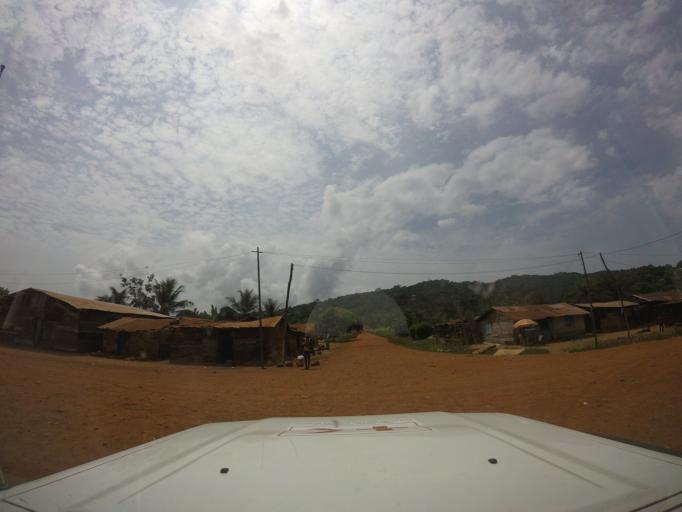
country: LR
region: Grand Cape Mount
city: Robertsport
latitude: 6.7566
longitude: -11.3722
